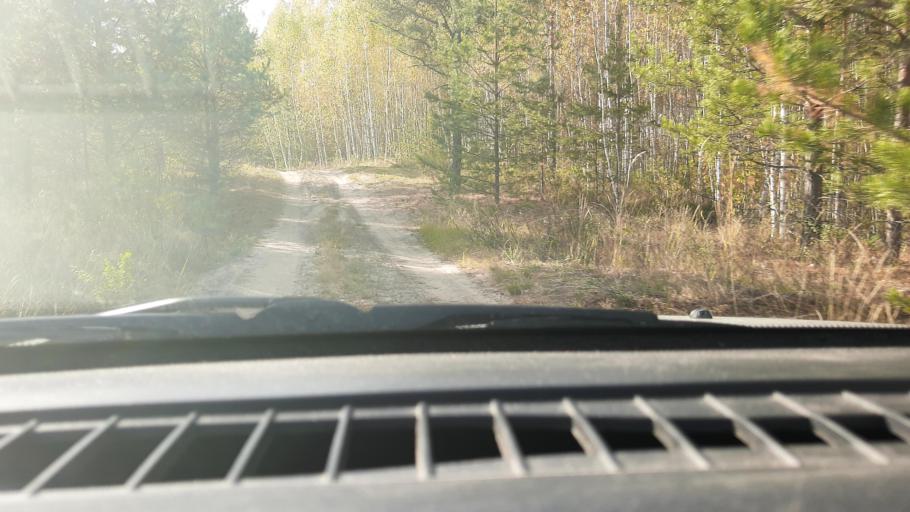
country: RU
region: Nizjnij Novgorod
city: Lukino
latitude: 56.3926
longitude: 43.5983
